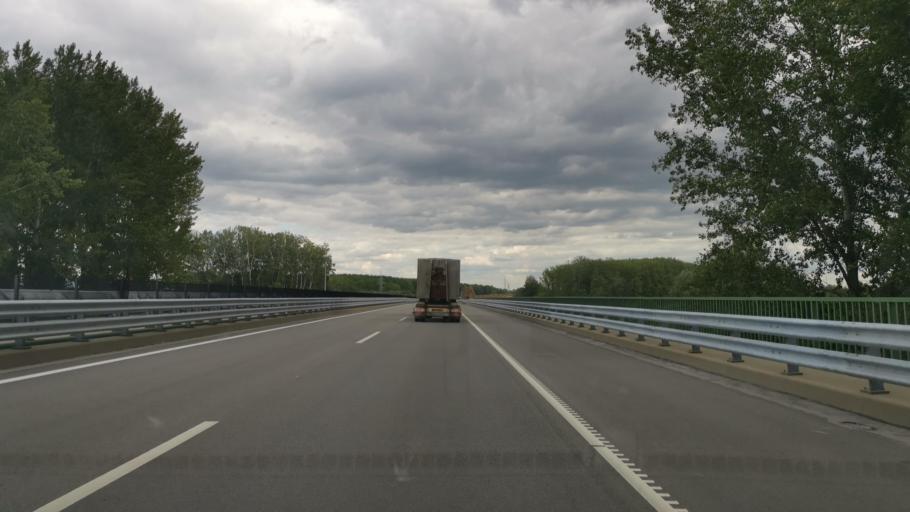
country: HU
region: Jasz-Nagykun-Szolnok
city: Tiszapuspoki
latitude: 47.2096
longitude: 20.2984
